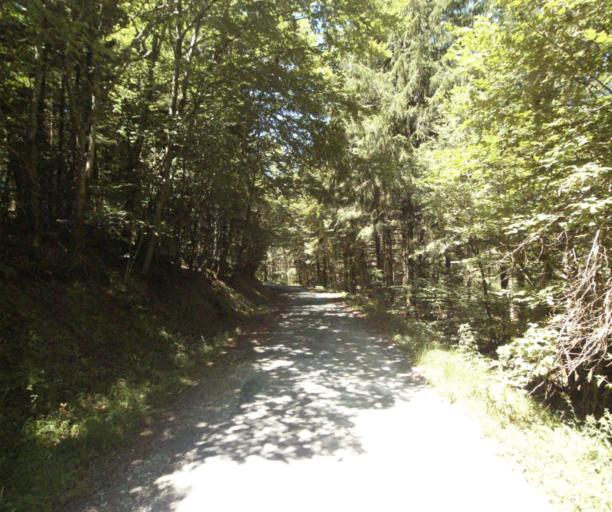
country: FR
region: Languedoc-Roussillon
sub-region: Departement de l'Aude
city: Cuxac-Cabardes
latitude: 43.4018
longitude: 2.2136
